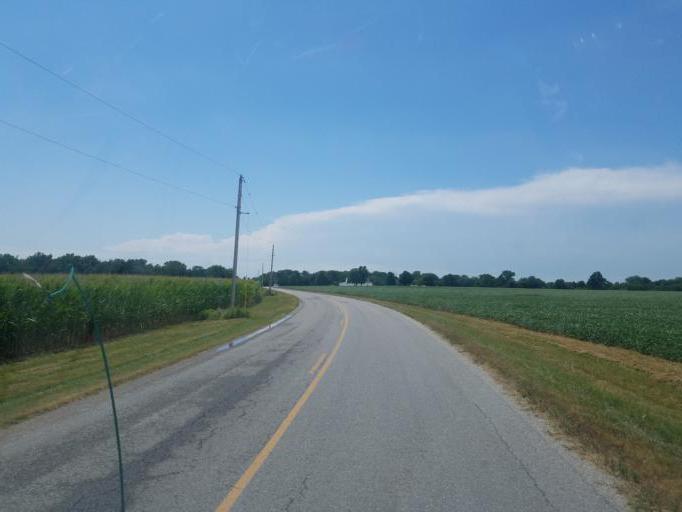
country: US
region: Ohio
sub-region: Paulding County
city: Antwerp
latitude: 41.1990
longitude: -84.7514
